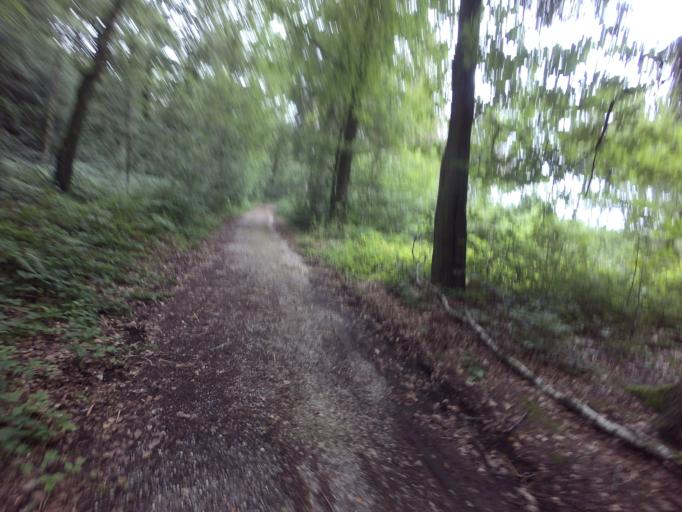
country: BE
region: Wallonia
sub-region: Province de Liege
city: Plombieres
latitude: 50.7636
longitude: 5.9805
